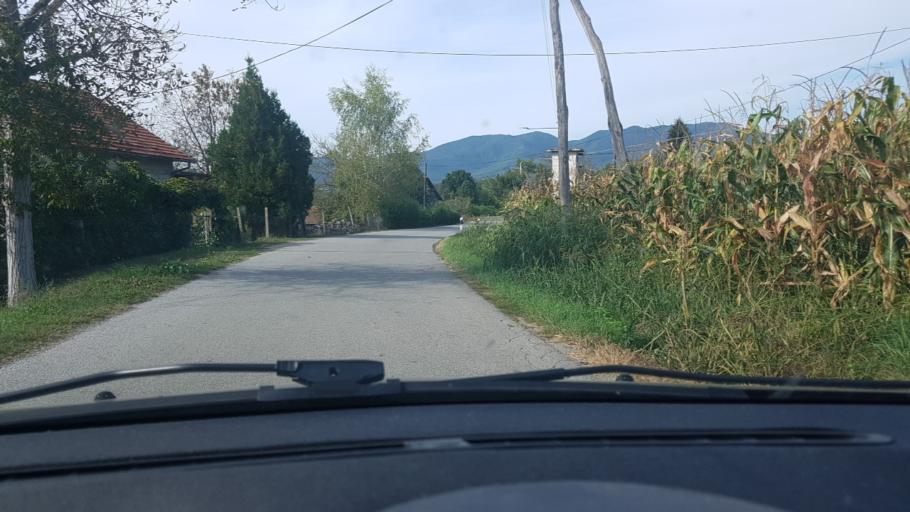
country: HR
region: Krapinsko-Zagorska
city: Zlatar
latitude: 46.1083
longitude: 16.1196
